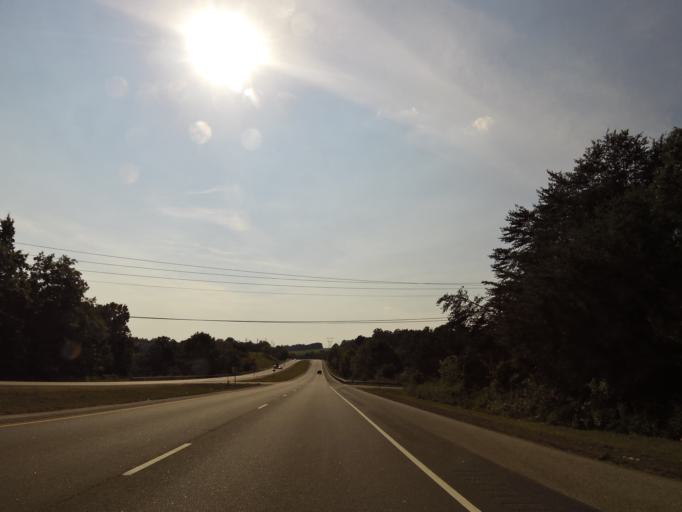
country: US
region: Tennessee
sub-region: Blount County
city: Louisville
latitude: 35.7583
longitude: -84.0592
